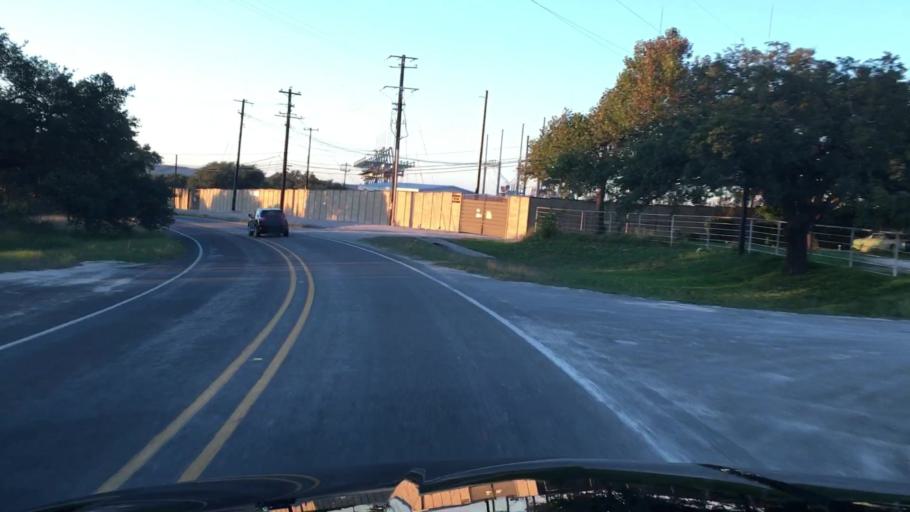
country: US
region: Texas
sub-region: Blanco County
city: Blanco
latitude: 30.0817
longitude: -98.4121
